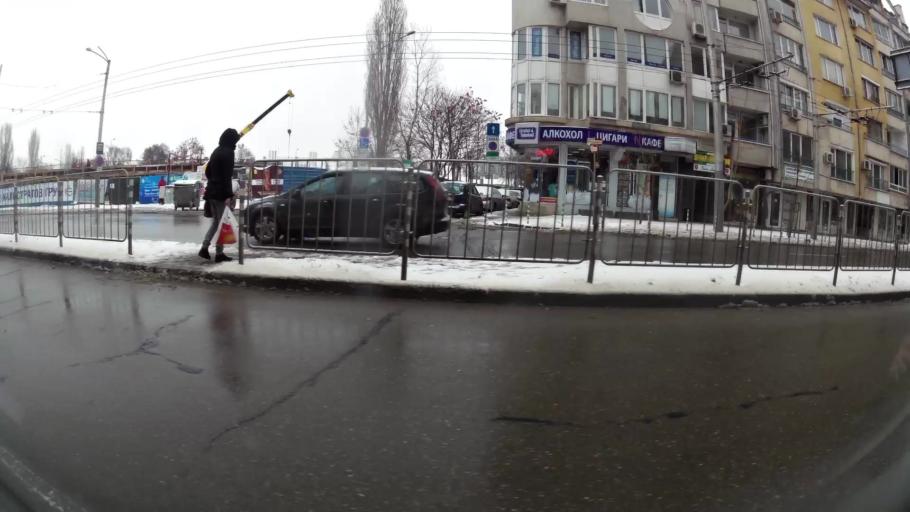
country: BG
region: Sofia-Capital
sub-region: Stolichna Obshtina
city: Sofia
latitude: 42.7040
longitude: 23.3330
